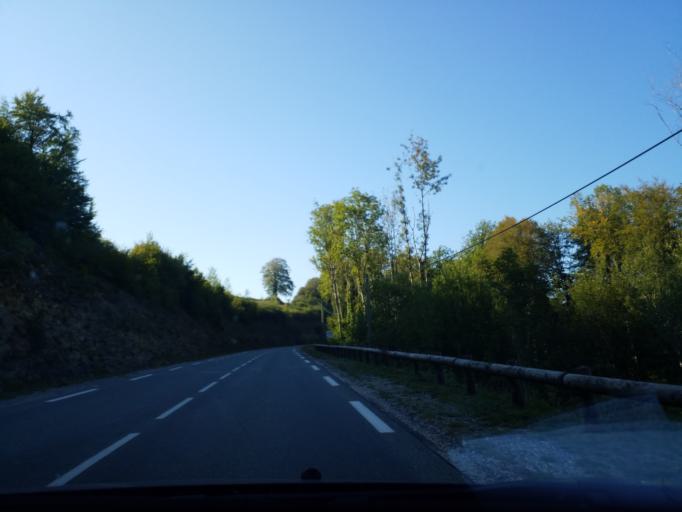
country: FR
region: Franche-Comte
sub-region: Departement du Doubs
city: Vercel-Villedieu-le-Camp
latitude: 47.2179
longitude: 6.3935
